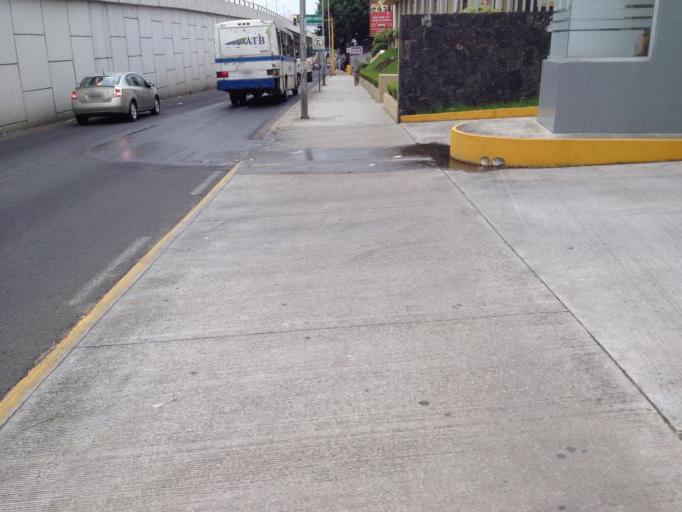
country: MX
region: Veracruz
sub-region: Xalapa
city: Xalapa de Enriquez
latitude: 19.5376
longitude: -96.9080
